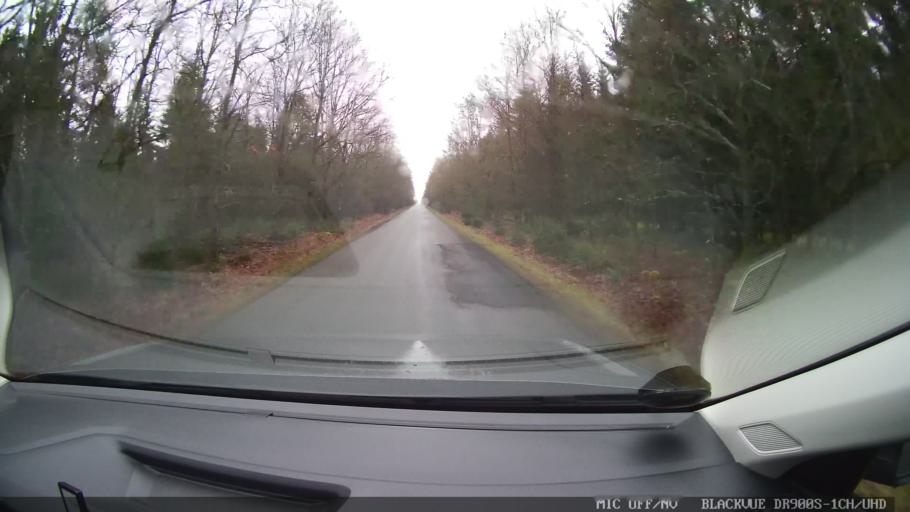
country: DK
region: Central Jutland
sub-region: Viborg Kommune
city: Karup
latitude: 56.2387
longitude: 9.1325
